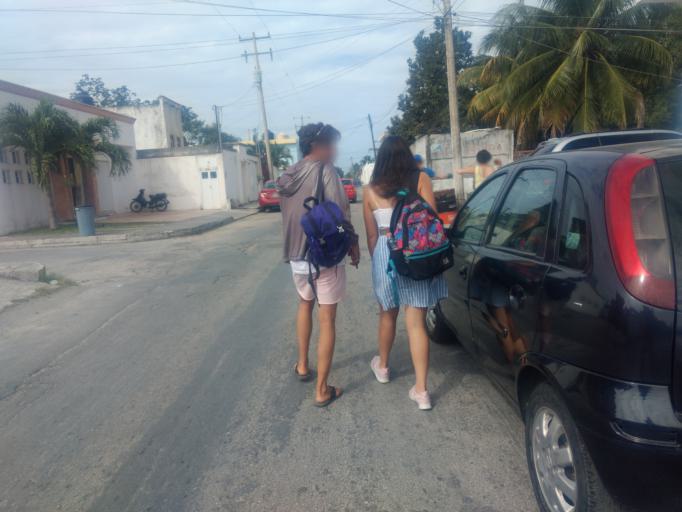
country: MX
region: Quintana Roo
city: San Miguel de Cozumel
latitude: 20.4992
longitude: -86.9369
